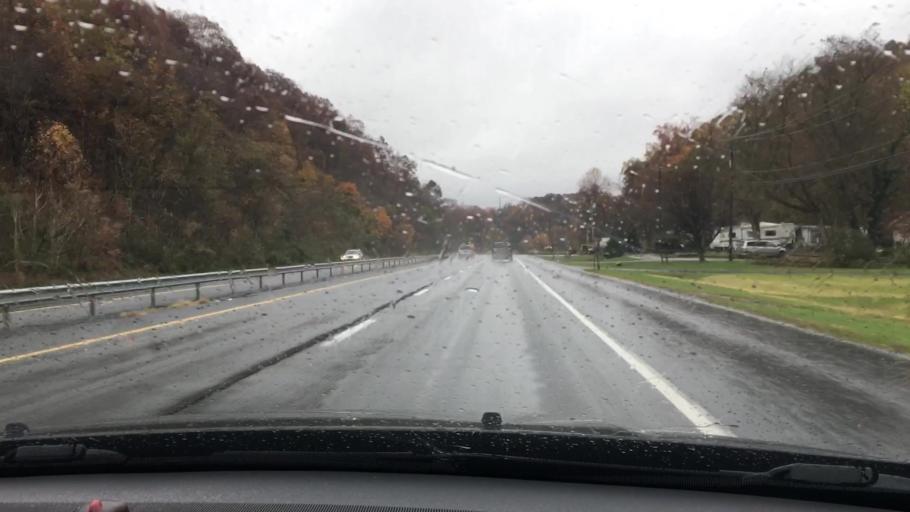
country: US
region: Pennsylvania
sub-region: Lancaster County
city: Willow Street
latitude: 39.9320
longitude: -76.2534
